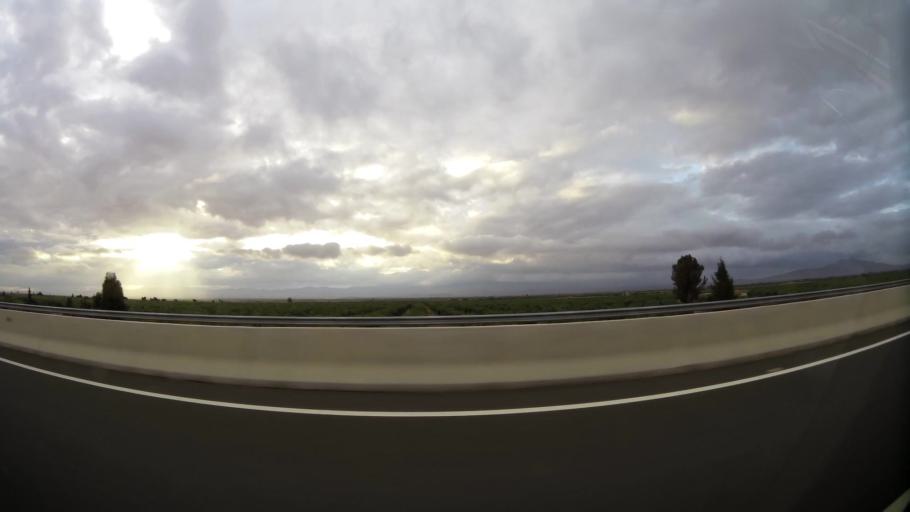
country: MA
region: Taza-Al Hoceima-Taounate
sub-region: Taza
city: Guercif
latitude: 34.3307
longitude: -3.3400
